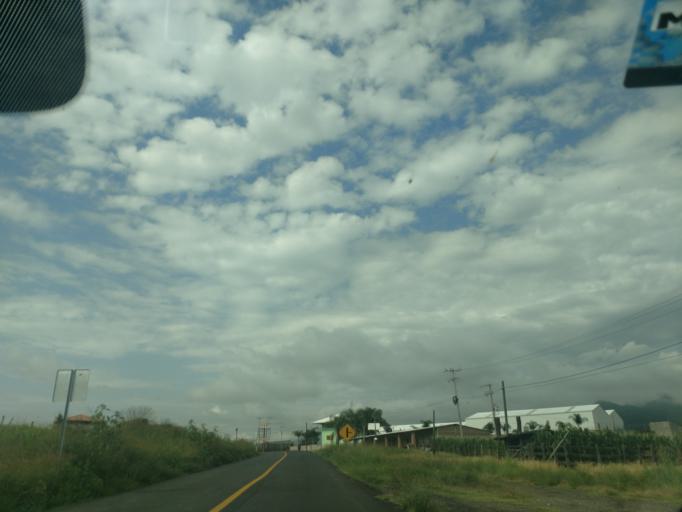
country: MX
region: Jalisco
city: El Salto
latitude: 20.4270
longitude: -104.4969
